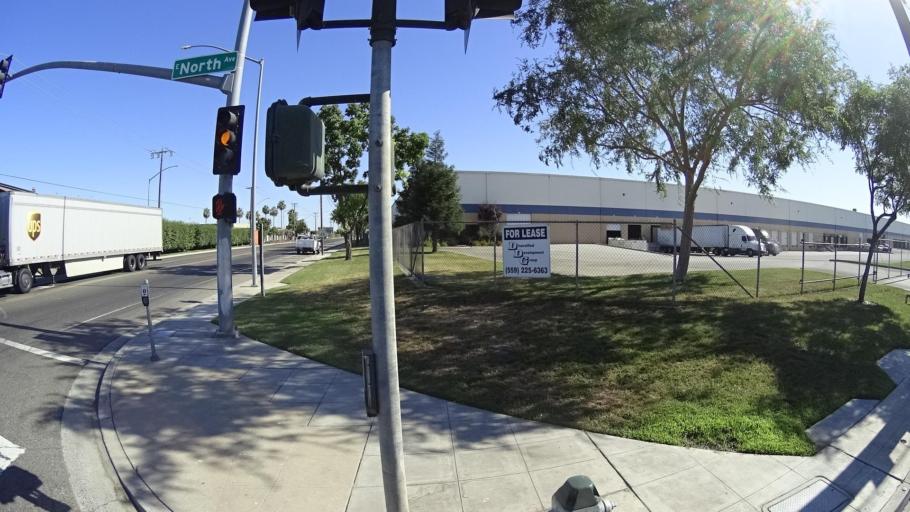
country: US
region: California
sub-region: Fresno County
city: Easton
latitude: 36.6924
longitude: -119.7816
